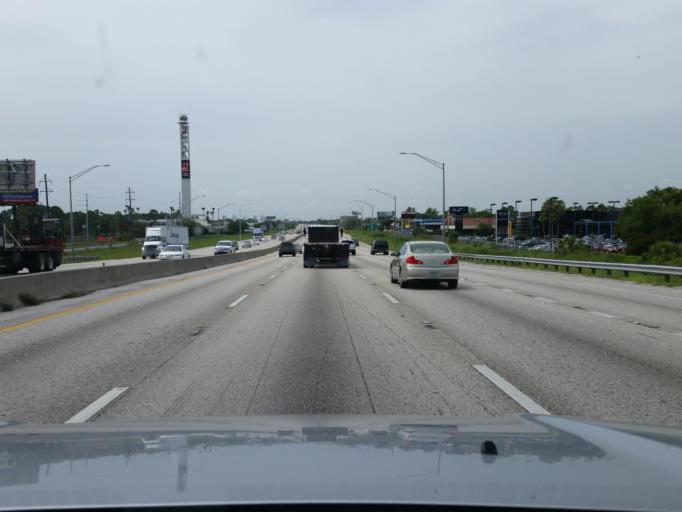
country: US
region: Florida
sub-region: Orange County
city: Eatonville
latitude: 28.6169
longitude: -81.3867
